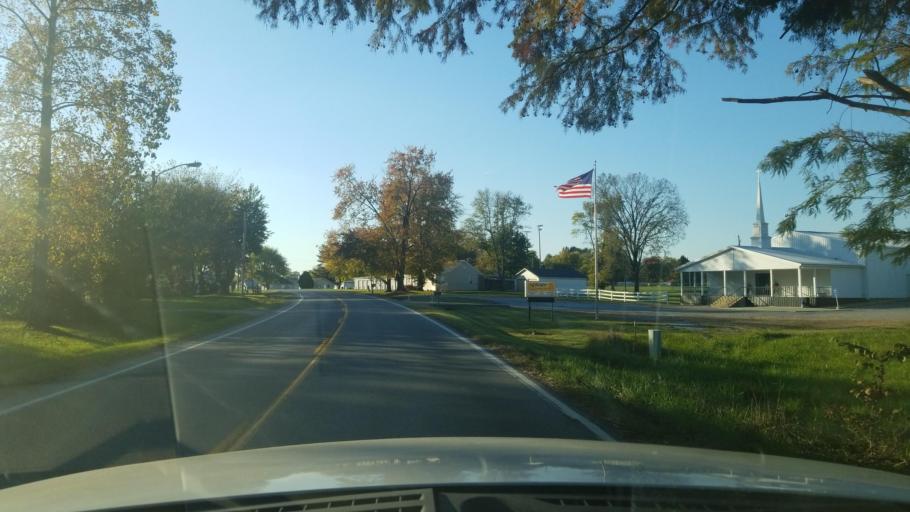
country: US
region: Illinois
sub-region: Saline County
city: Harrisburg
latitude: 37.8405
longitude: -88.6030
